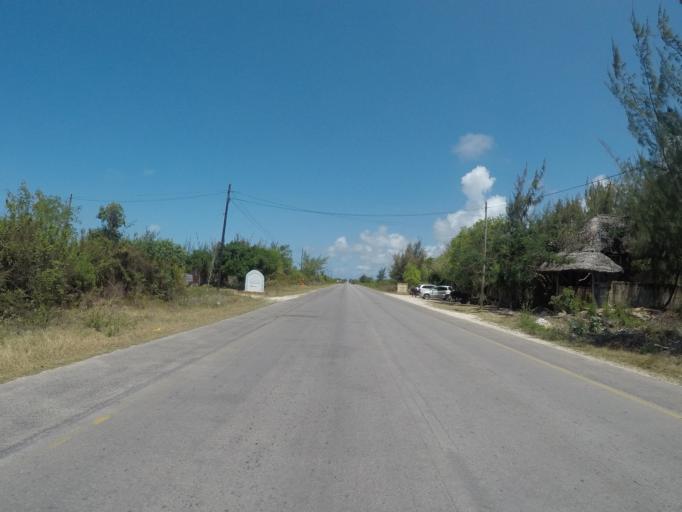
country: TZ
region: Zanzibar Central/South
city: Nganane
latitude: -6.2874
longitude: 39.5365
